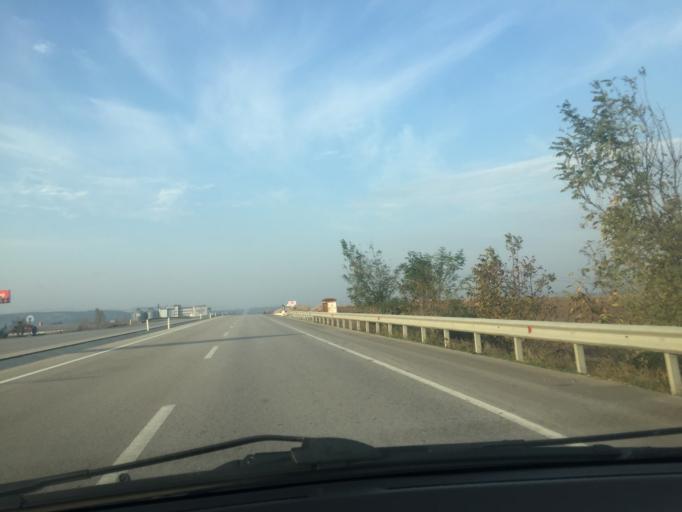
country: TR
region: Canakkale
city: Sinekci
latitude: 40.2585
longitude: 27.3435
